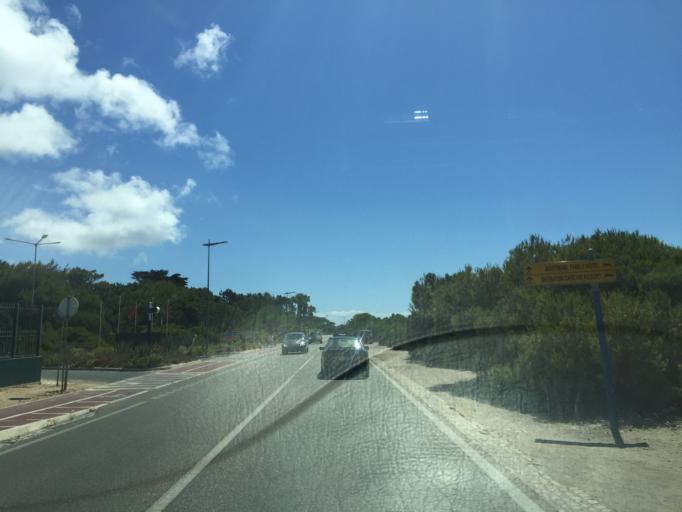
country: PT
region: Lisbon
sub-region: Cascais
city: Cascais
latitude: 38.6979
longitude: -9.4641
